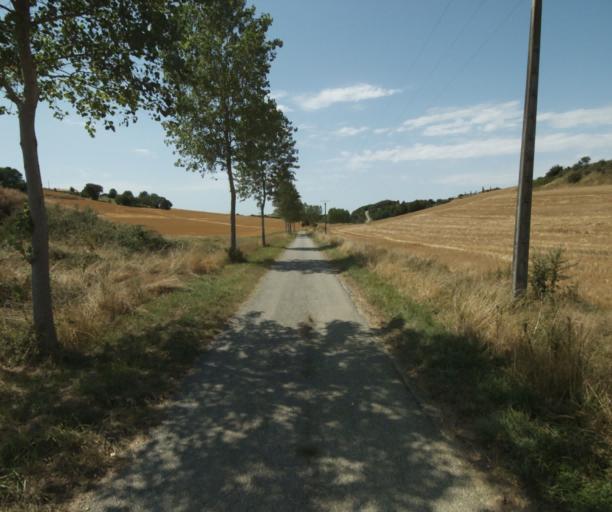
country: FR
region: Midi-Pyrenees
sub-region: Departement de la Haute-Garonne
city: Saint-Felix-Lauragais
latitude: 43.4612
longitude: 1.8657
